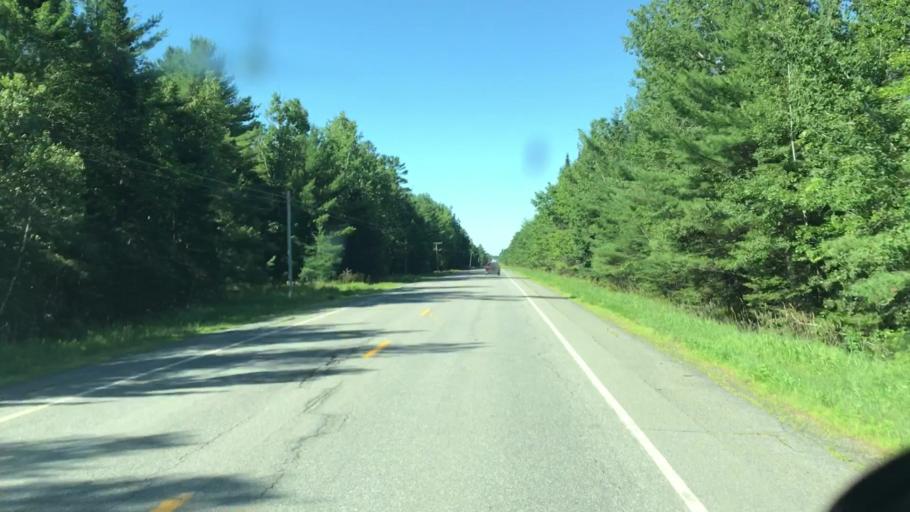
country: US
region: Maine
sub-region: Penobscot County
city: Enfield
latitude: 45.3141
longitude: -68.6048
